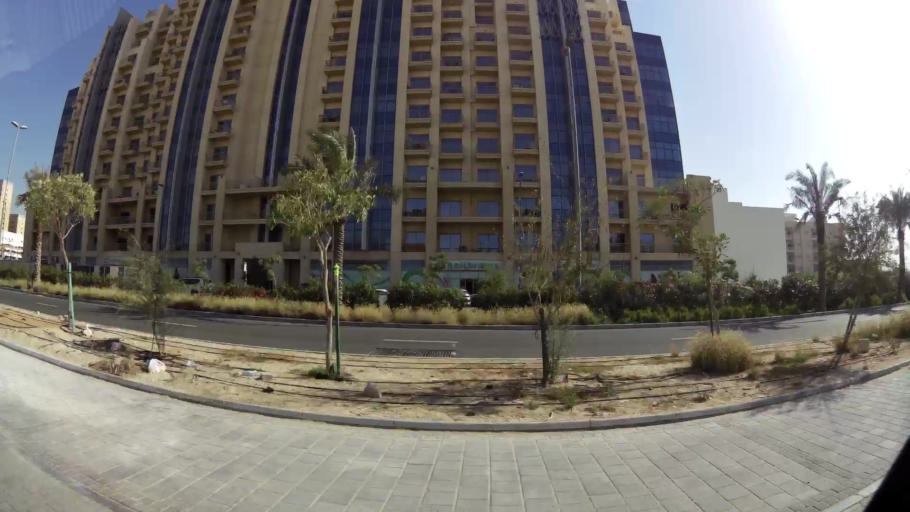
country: AE
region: Dubai
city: Dubai
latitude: 25.0695
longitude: 55.2075
